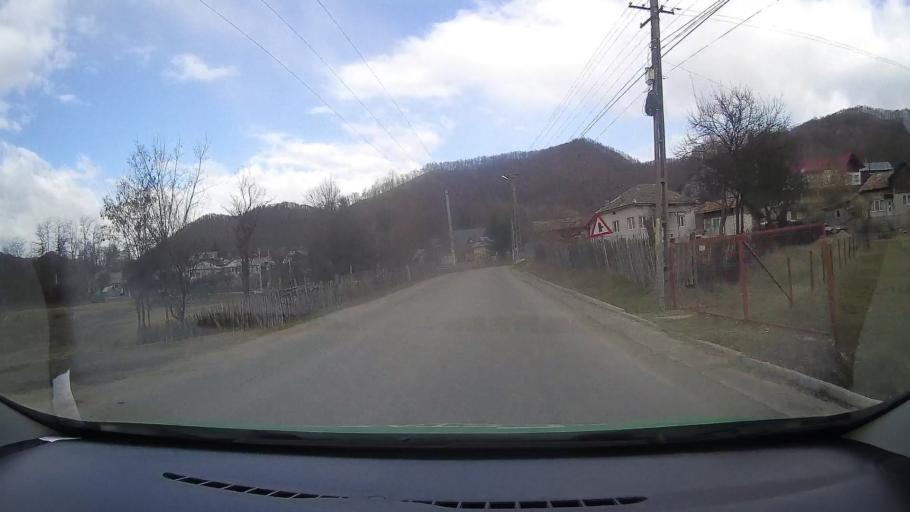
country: RO
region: Dambovita
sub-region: Comuna Varfuri
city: Varfuri
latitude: 45.0761
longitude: 25.5265
